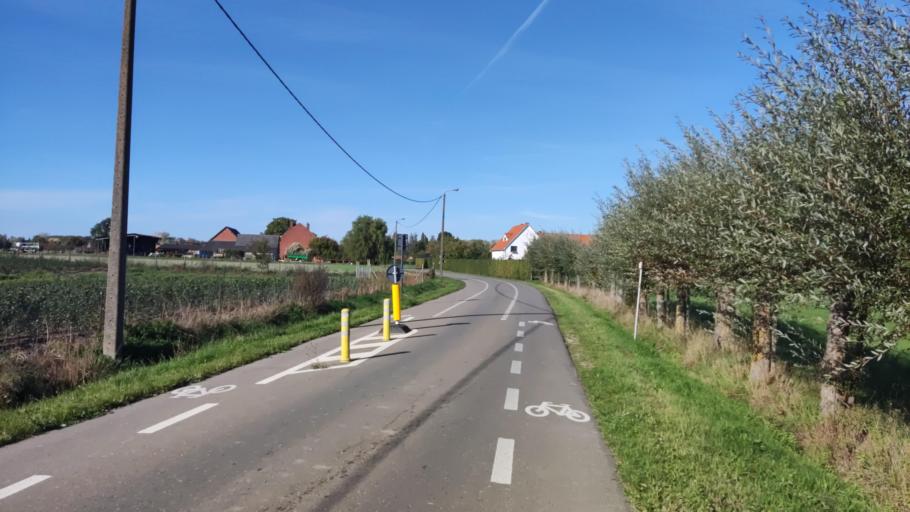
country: BE
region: Flanders
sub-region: Provincie Limburg
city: Alken
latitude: 50.9208
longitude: 5.2685
